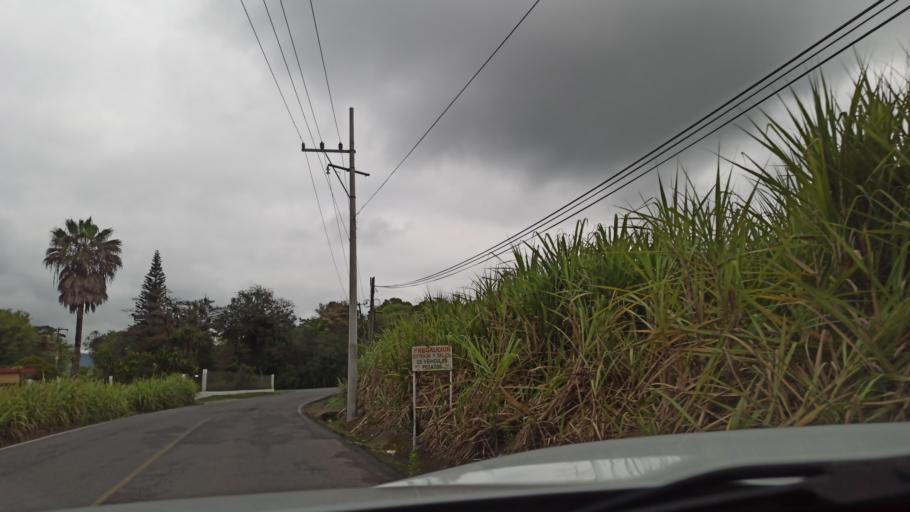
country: MX
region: Veracruz
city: Chocaman
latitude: 19.0109
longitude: -97.0161
